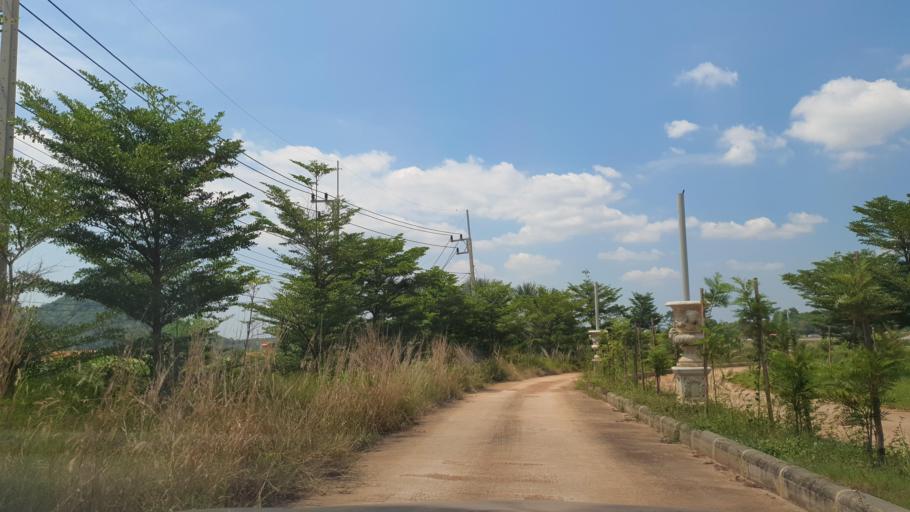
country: TH
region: Rayong
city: Ban Chang
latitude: 12.7526
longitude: 100.9634
